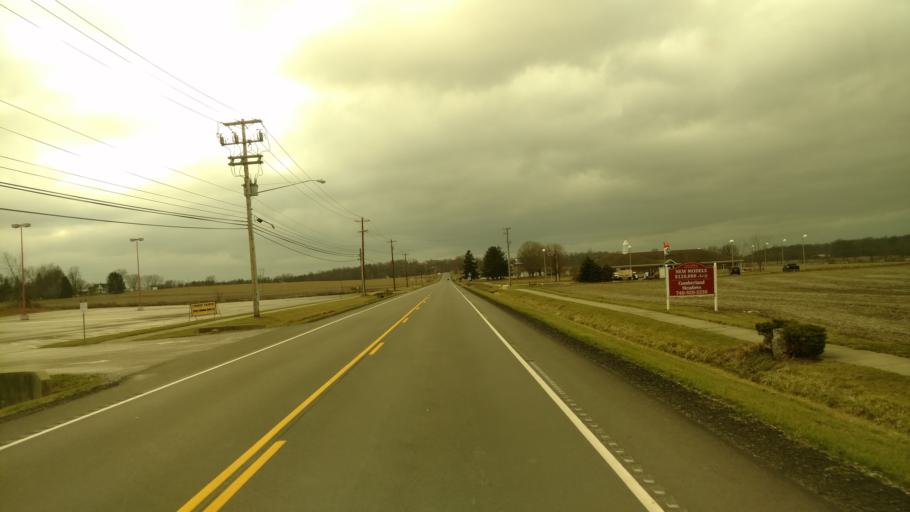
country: US
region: Ohio
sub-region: Licking County
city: Hebron
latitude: 39.9601
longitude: -82.5017
